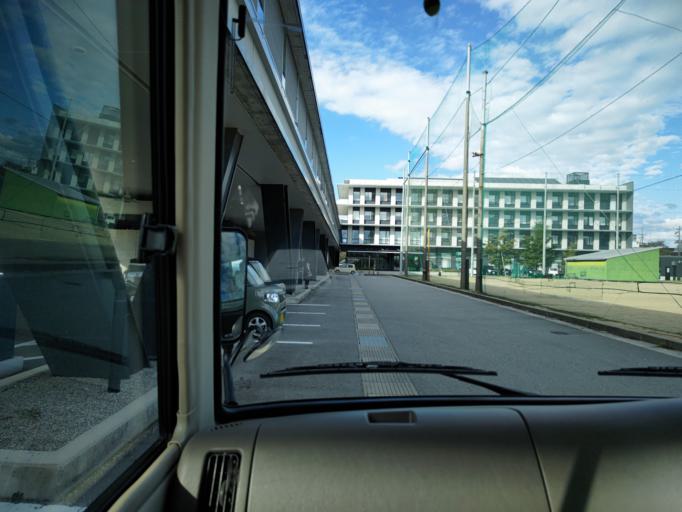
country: JP
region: Toyama
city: Uozu
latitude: 36.8706
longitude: 137.4476
